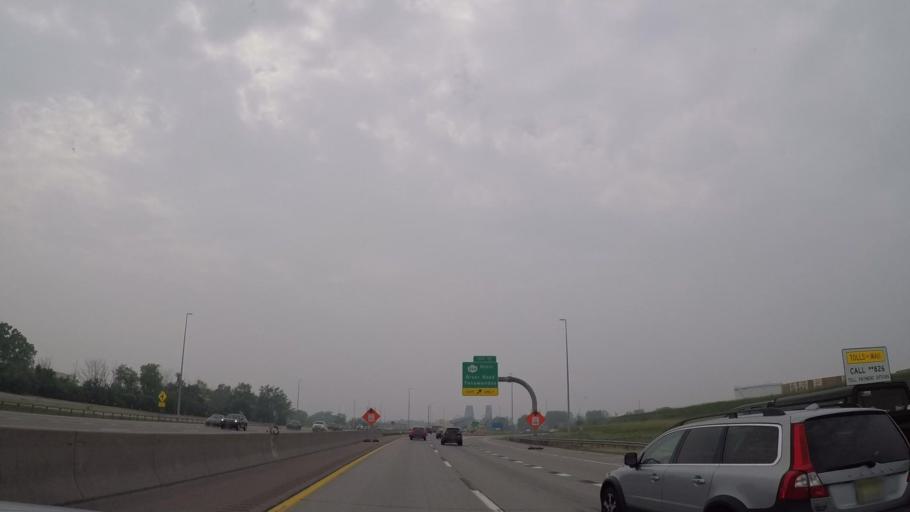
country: US
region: New York
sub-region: Erie County
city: Grandyle Village
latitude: 42.9927
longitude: -78.9259
